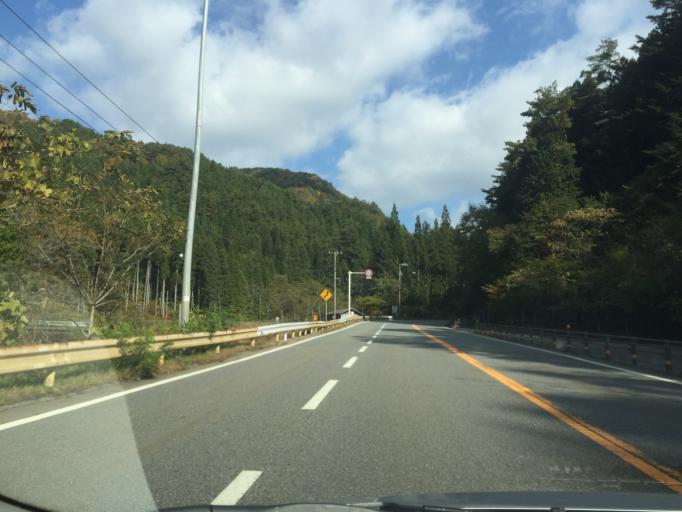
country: JP
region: Gifu
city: Nakatsugawa
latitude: 35.2919
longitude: 137.6022
